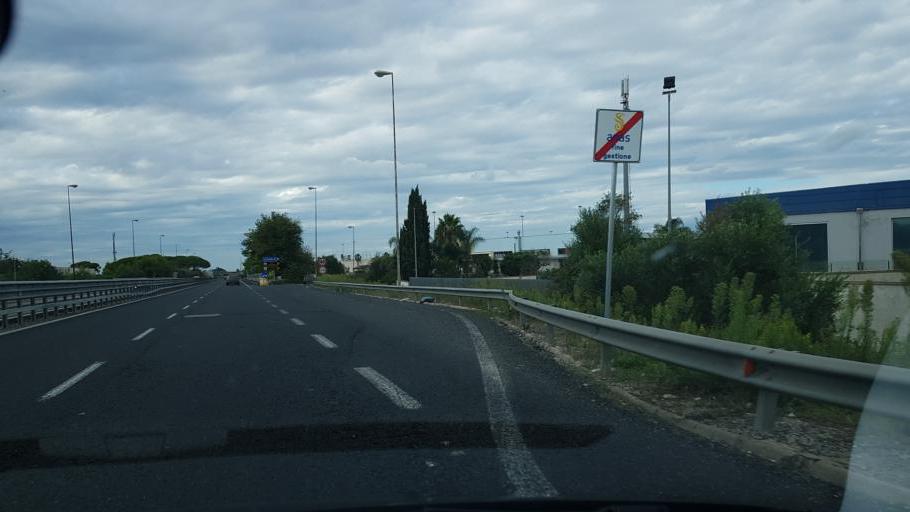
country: IT
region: Apulia
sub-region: Provincia di Lecce
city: Cavallino
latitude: 40.2891
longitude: 18.1983
